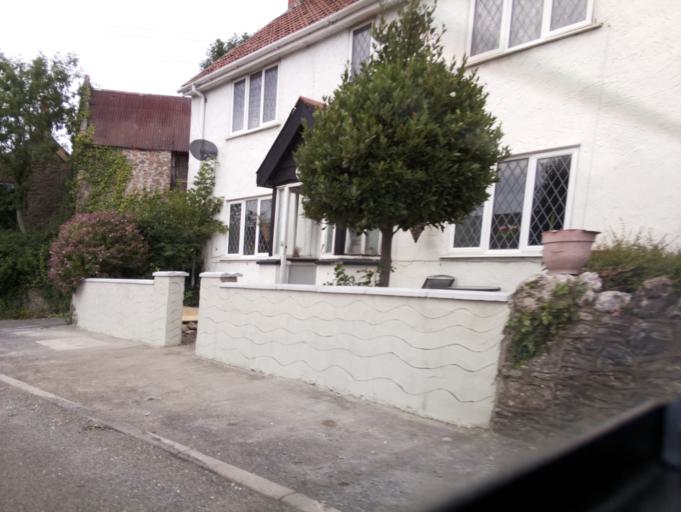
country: GB
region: England
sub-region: Somerset
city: Wells
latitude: 51.2271
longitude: -2.7007
